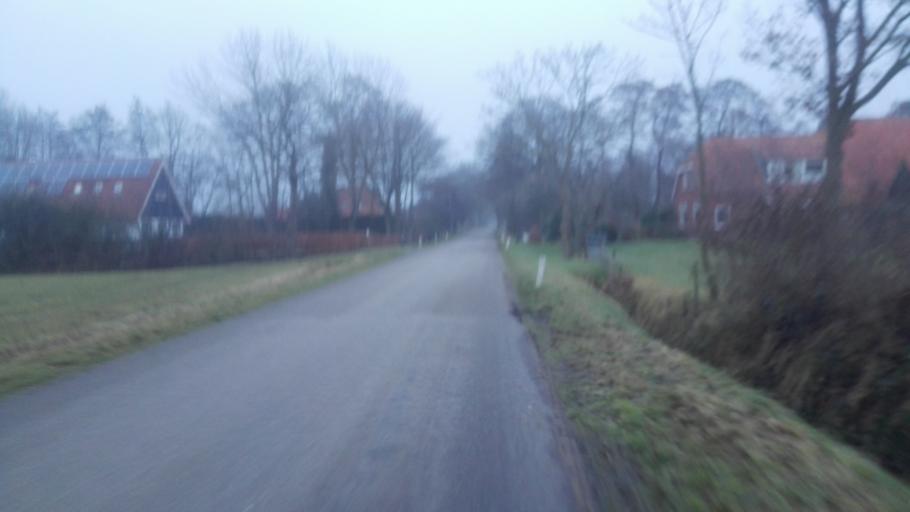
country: NL
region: Friesland
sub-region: Gemeente Heerenveen
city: Jubbega
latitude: 52.9529
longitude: 6.1584
